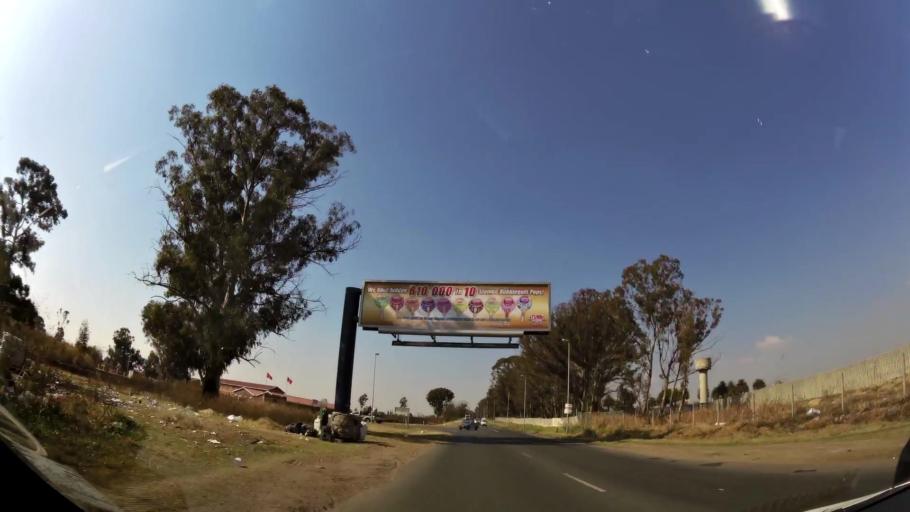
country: ZA
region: Gauteng
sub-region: Ekurhuleni Metropolitan Municipality
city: Benoni
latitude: -26.2079
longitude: 28.3141
